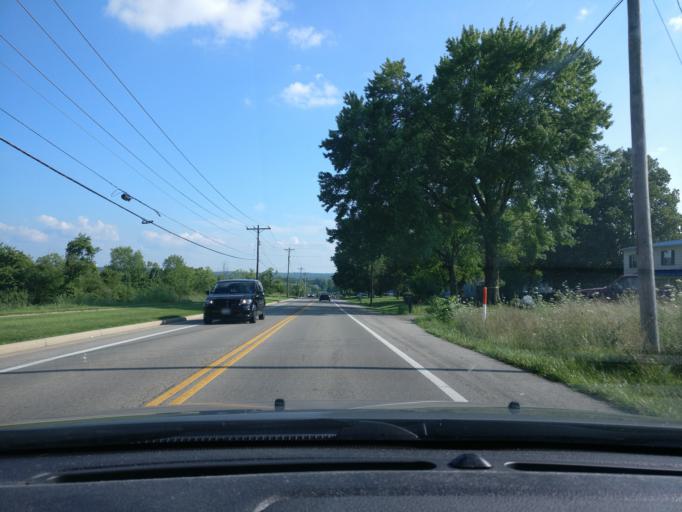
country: US
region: Ohio
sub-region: Warren County
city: Springboro
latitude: 39.5671
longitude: -84.2521
